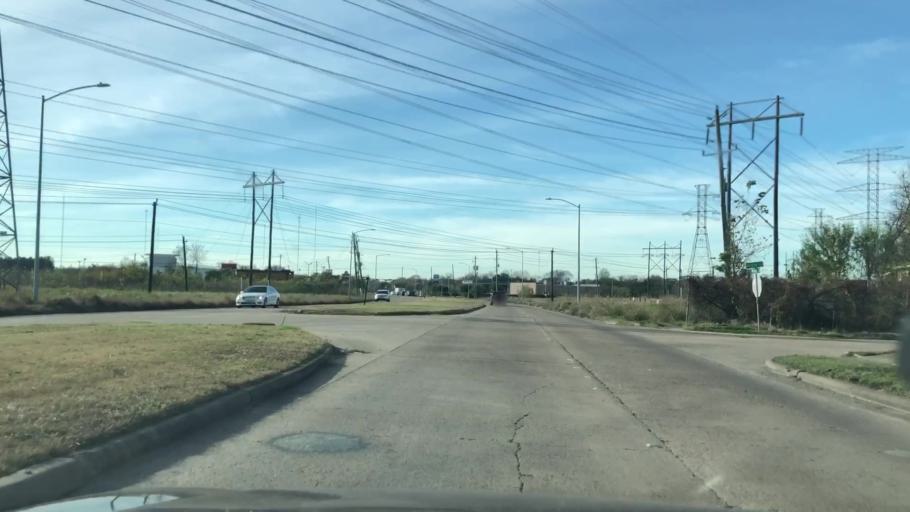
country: US
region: Texas
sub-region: Fort Bend County
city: Missouri City
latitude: 29.6296
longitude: -95.4942
